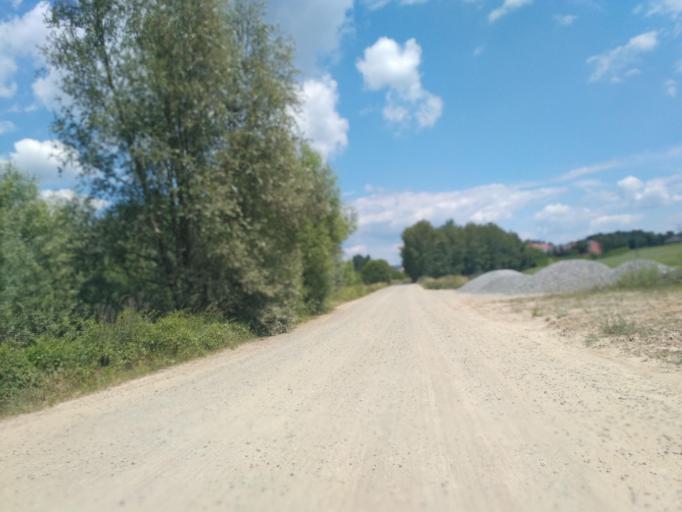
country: PL
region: Subcarpathian Voivodeship
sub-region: Powiat debicki
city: Brzostek
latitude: 49.8561
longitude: 21.4061
